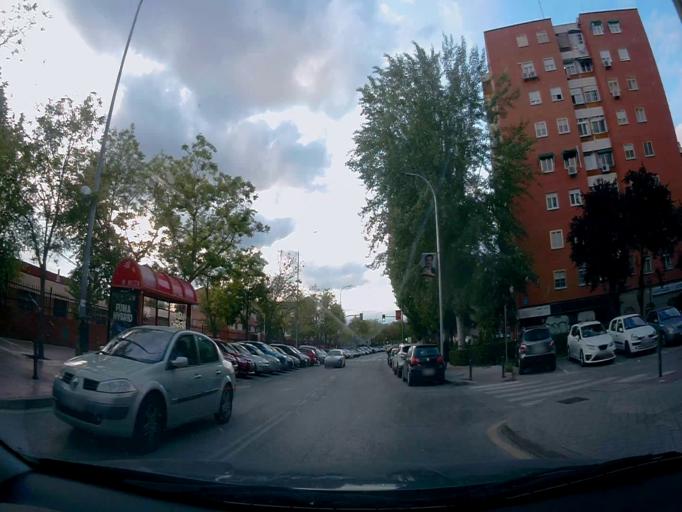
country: ES
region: Madrid
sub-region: Provincia de Madrid
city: Mostoles
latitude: 40.3200
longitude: -3.8796
